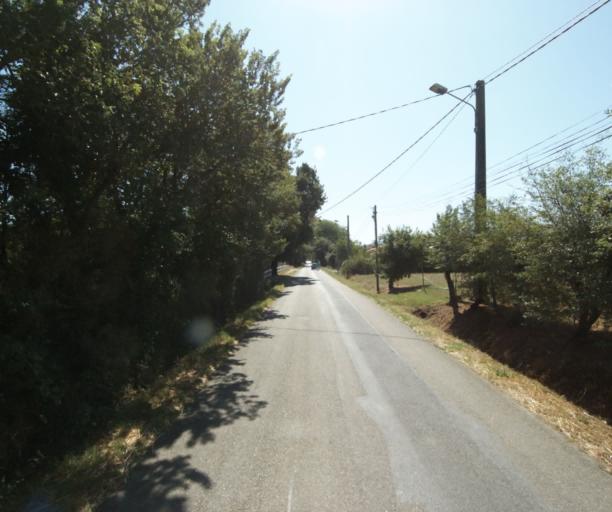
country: FR
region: Midi-Pyrenees
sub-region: Departement de la Haute-Garonne
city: Revel
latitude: 43.4692
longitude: 1.9988
